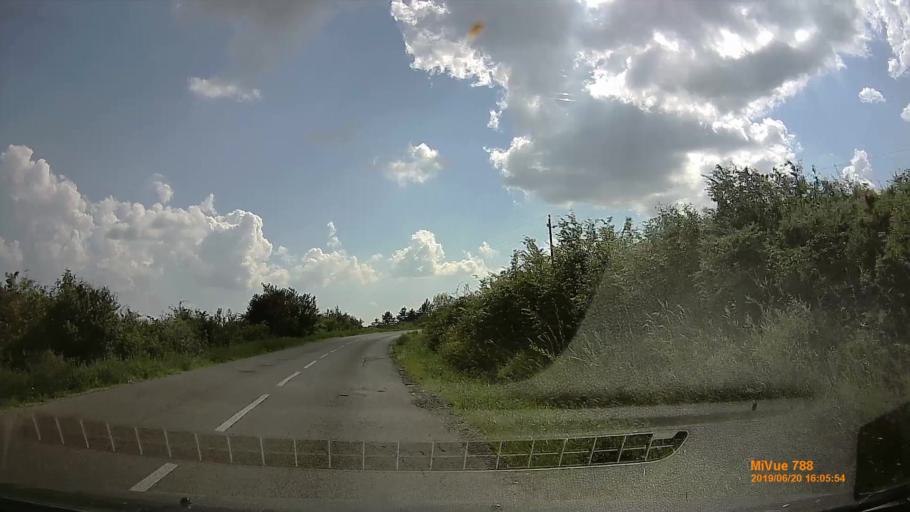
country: HU
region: Baranya
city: Pellerd
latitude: 46.0795
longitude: 18.1150
